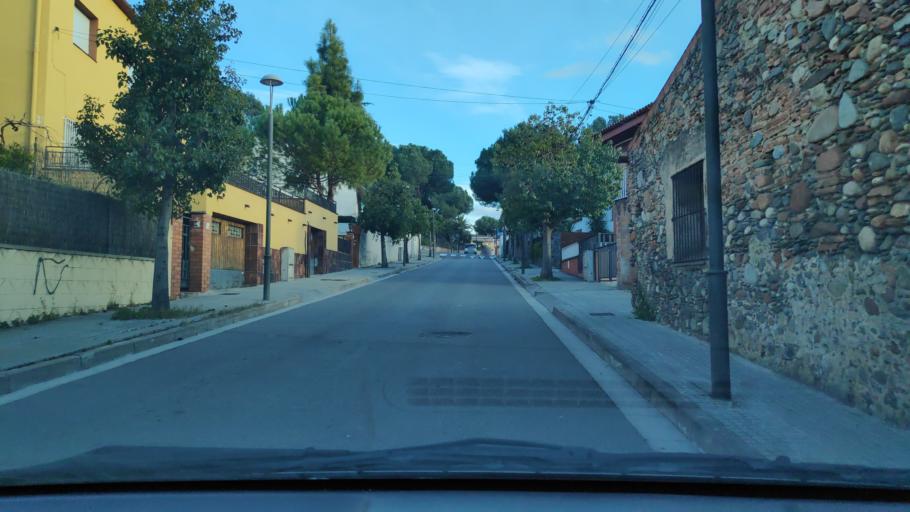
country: ES
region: Catalonia
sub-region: Provincia de Barcelona
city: Montmelo
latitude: 41.5545
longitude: 2.2443
